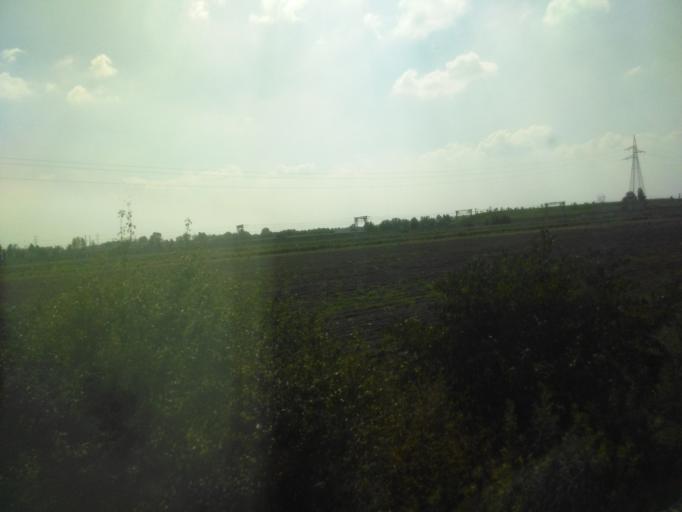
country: IT
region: Lombardy
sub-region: Provincia di Bergamo
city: Casirate d'Adda
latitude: 45.5126
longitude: 9.5441
